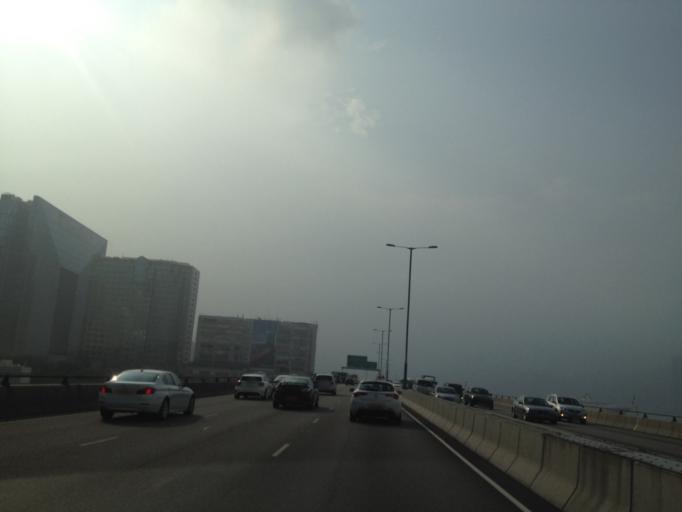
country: HK
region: Kowloon City
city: Kowloon
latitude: 22.3096
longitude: 114.2196
